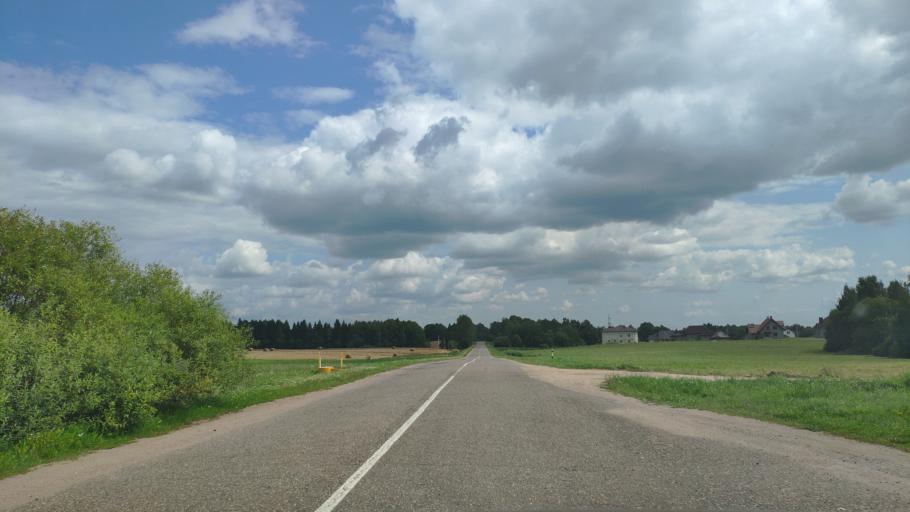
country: BY
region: Minsk
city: Khatsyezhyna
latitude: 53.8816
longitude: 27.2774
